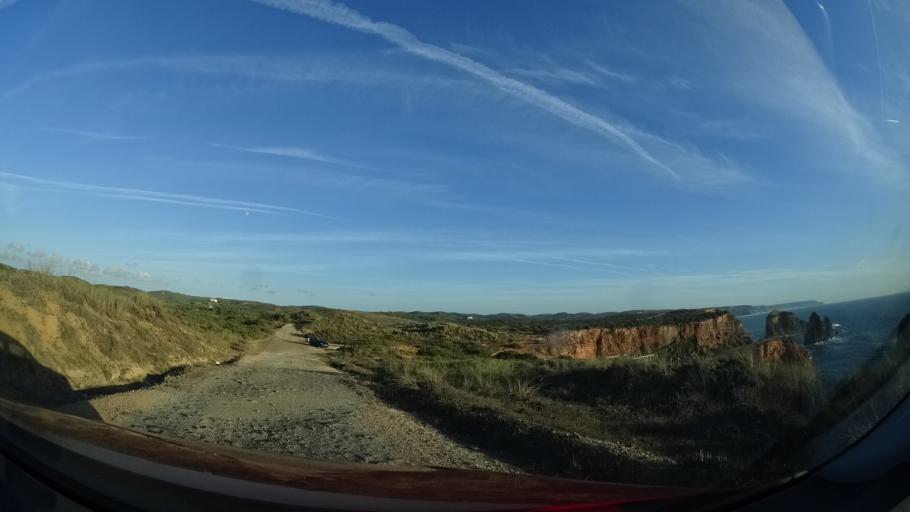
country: PT
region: Faro
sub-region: Vila do Bispo
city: Vila do Bispo
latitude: 37.1819
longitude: -8.9093
